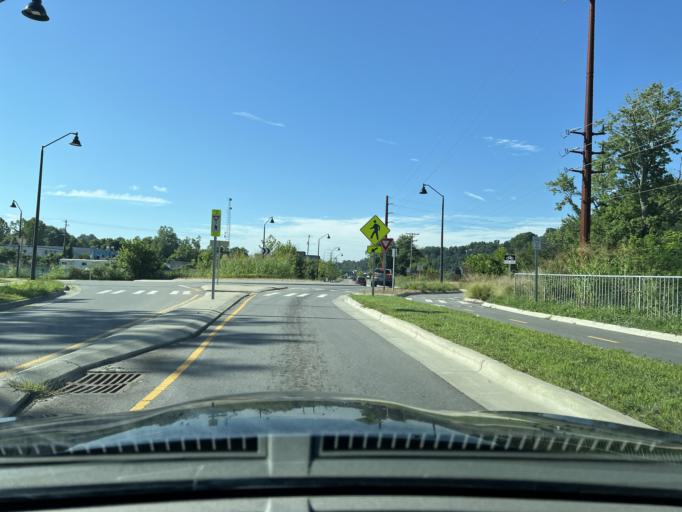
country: US
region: North Carolina
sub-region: Buncombe County
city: Asheville
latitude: 35.5848
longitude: -82.5672
